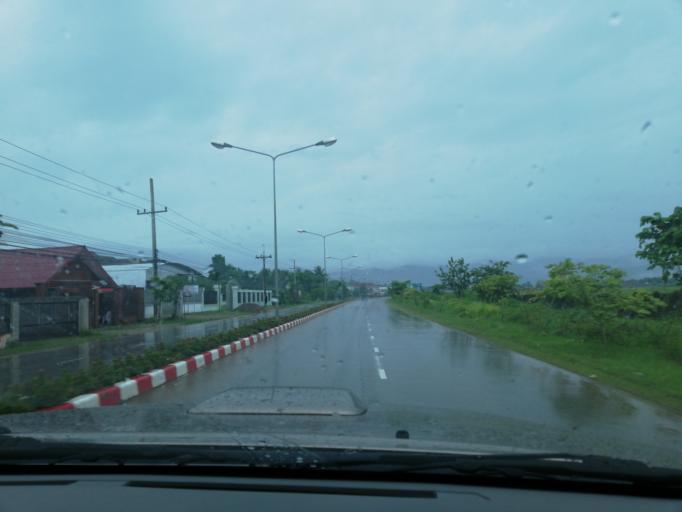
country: LA
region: Loungnamtha
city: Louang Namtha
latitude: 20.9569
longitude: 101.4039
